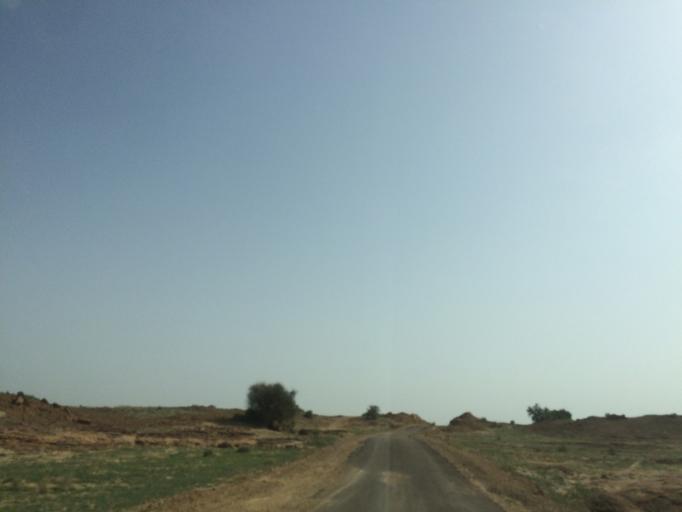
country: IN
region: Rajasthan
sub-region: Jaisalmer
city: Jaisalmer
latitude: 26.9041
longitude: 70.7823
